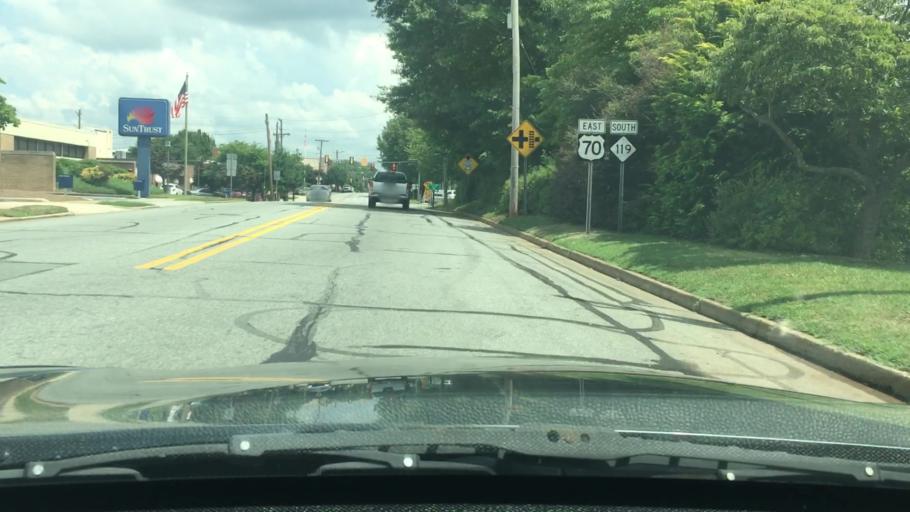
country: US
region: North Carolina
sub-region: Alamance County
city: Mebane
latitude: 36.0971
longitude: -79.2710
